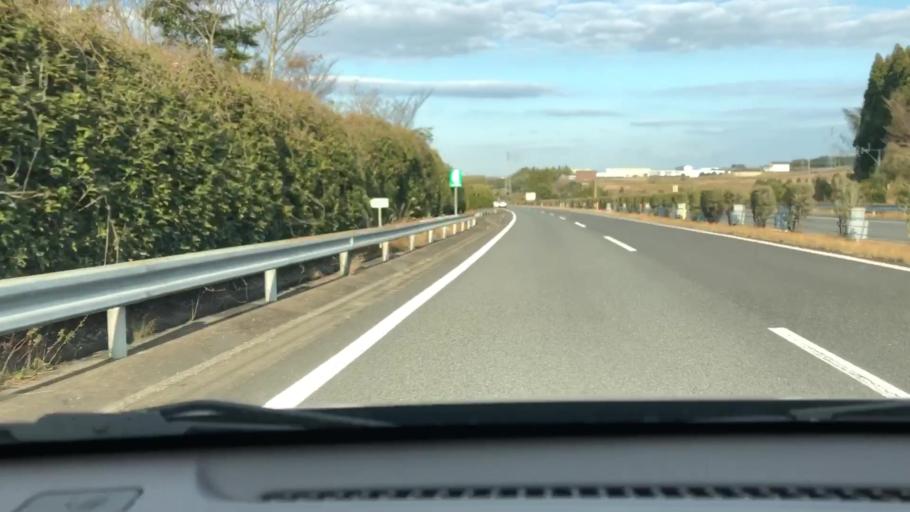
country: JP
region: Miyazaki
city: Miyazaki-shi
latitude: 31.8235
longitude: 131.3063
